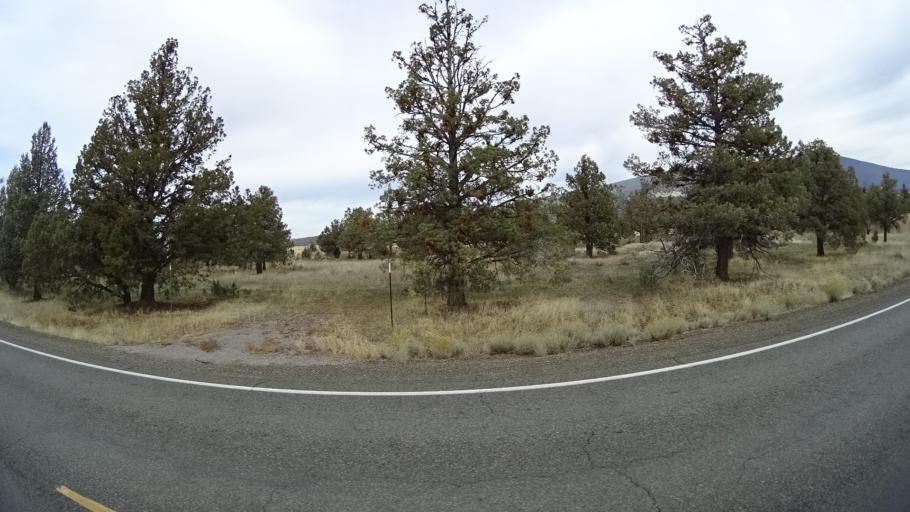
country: US
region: California
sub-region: Siskiyou County
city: Weed
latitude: 41.5935
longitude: -122.3156
